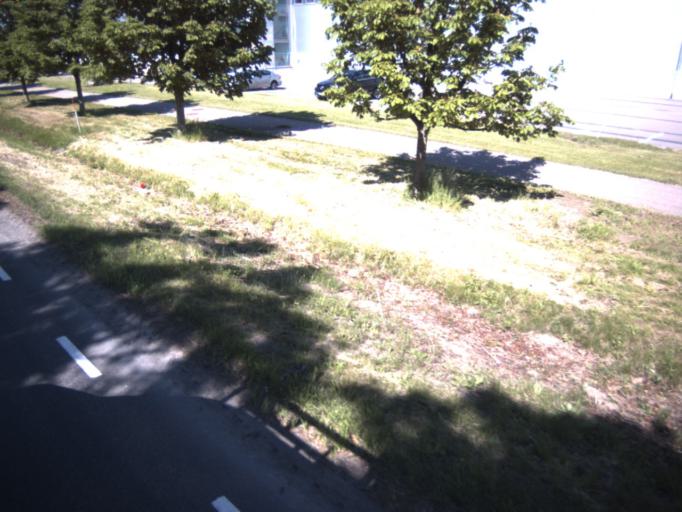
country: SE
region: Skane
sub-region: Helsingborg
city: Barslov
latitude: 56.0426
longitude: 12.7791
